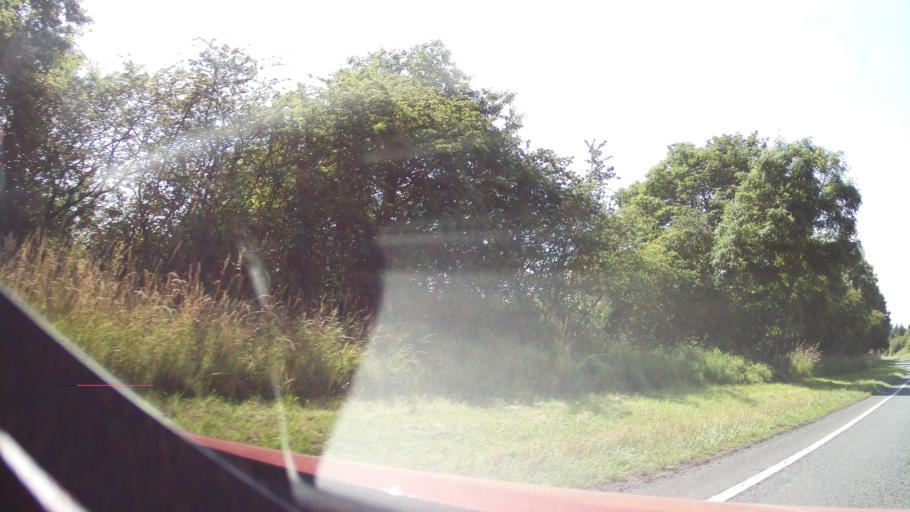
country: GB
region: England
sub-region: Worcestershire
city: Barnt Green
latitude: 52.3218
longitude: -2.0040
